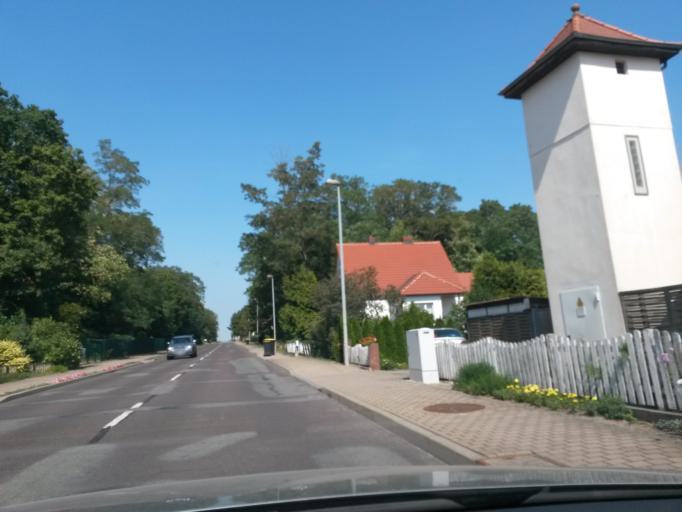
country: DE
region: Saxony-Anhalt
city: Jerichow
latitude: 52.3947
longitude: 11.9943
